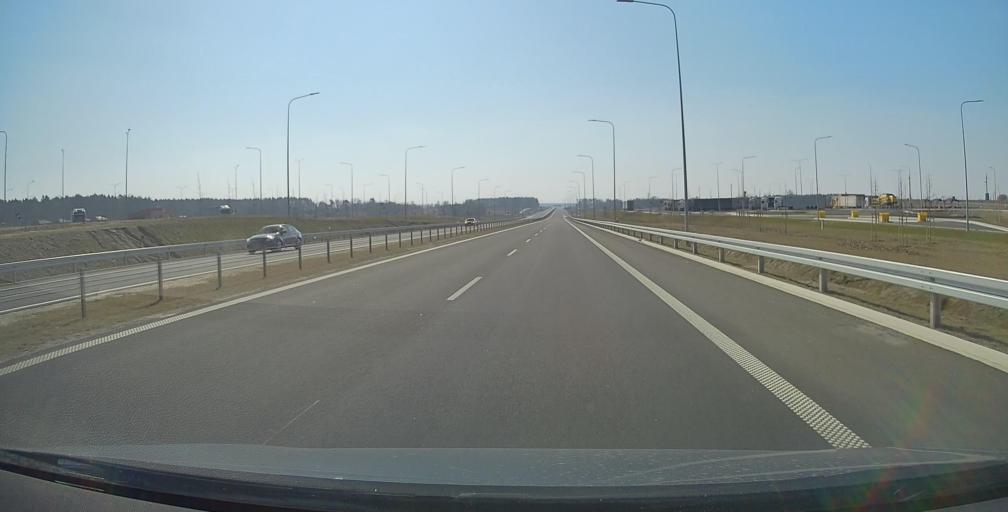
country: PL
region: Lublin Voivodeship
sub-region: Powiat janowski
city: Modliborzyce
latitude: 50.7833
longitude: 22.2916
